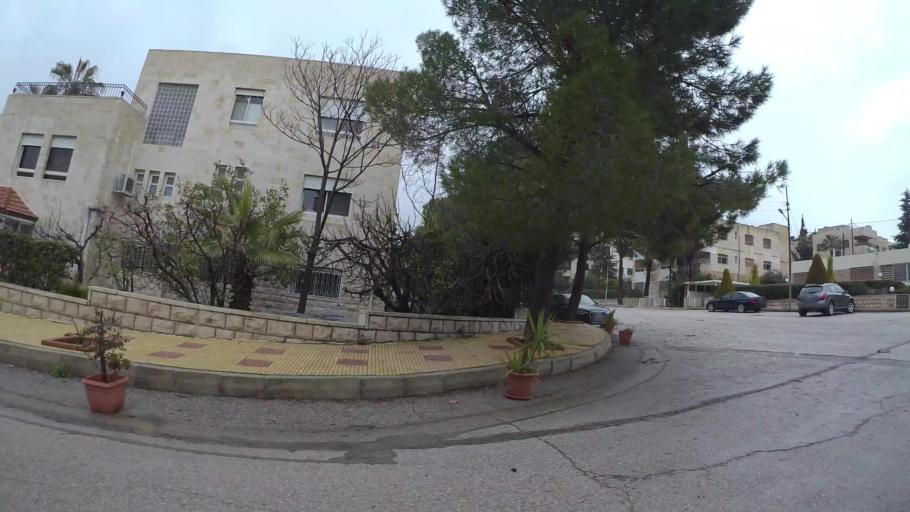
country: JO
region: Amman
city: Wadi as Sir
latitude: 31.9671
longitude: 35.8462
